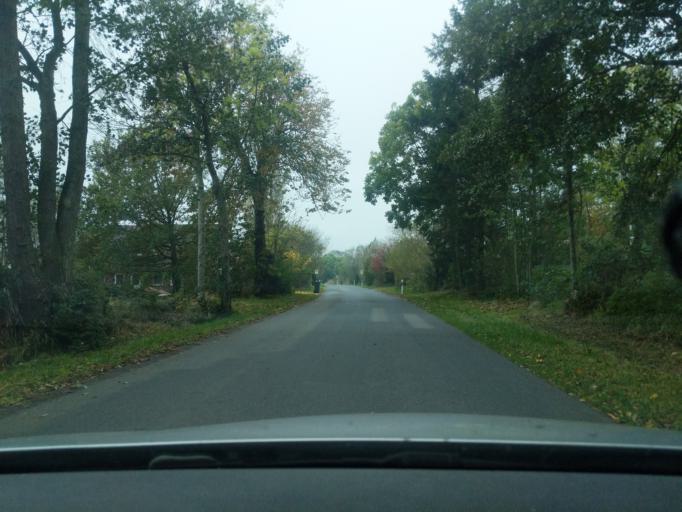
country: DE
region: Lower Saxony
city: Nordleda
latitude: 53.8281
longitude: 8.8113
